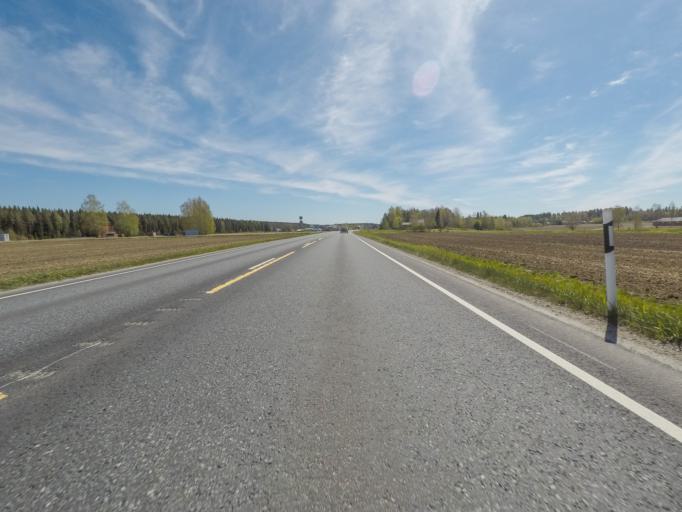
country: FI
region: Haeme
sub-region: Forssa
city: Humppila
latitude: 60.9471
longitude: 23.3535
